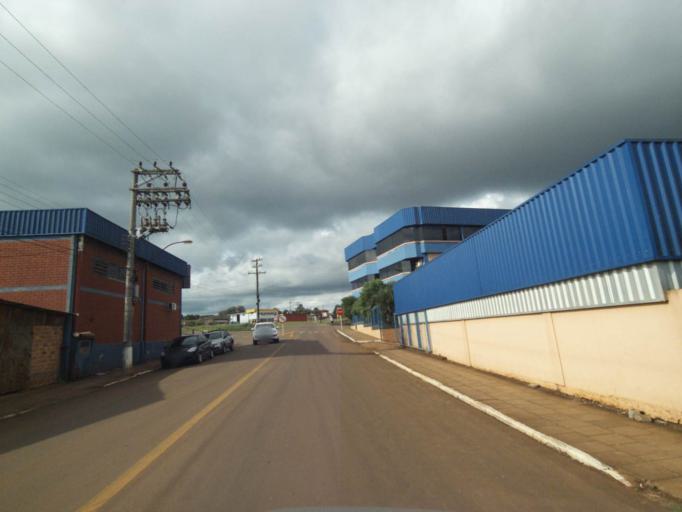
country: BR
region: Rio Grande do Sul
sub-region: Lagoa Vermelha
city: Lagoa Vermelha
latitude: -28.2055
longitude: -51.5313
